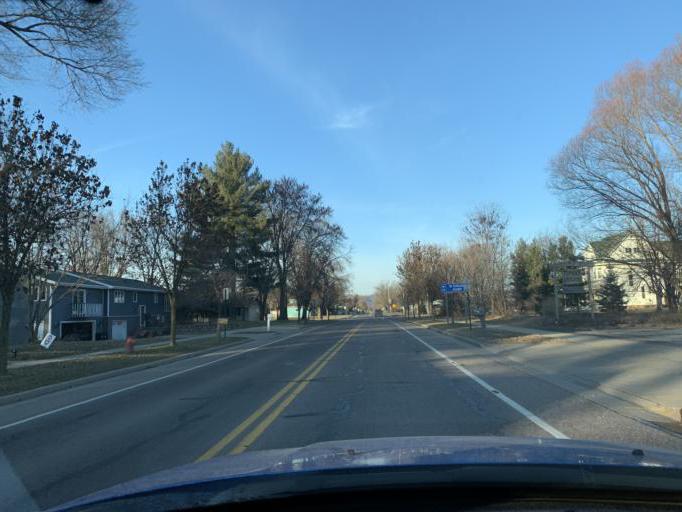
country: US
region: Wisconsin
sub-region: Sauk County
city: Spring Green
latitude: 43.1742
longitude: -90.0640
